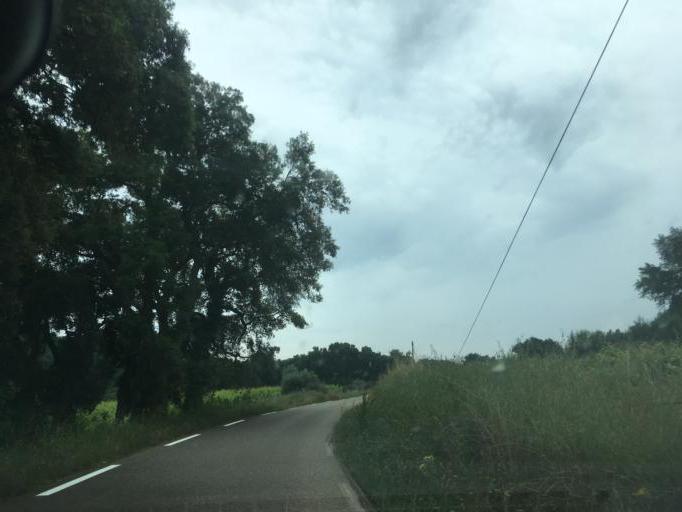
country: FR
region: Provence-Alpes-Cote d'Azur
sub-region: Departement du Var
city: La Londe-les-Maures
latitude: 43.1763
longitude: 6.2153
